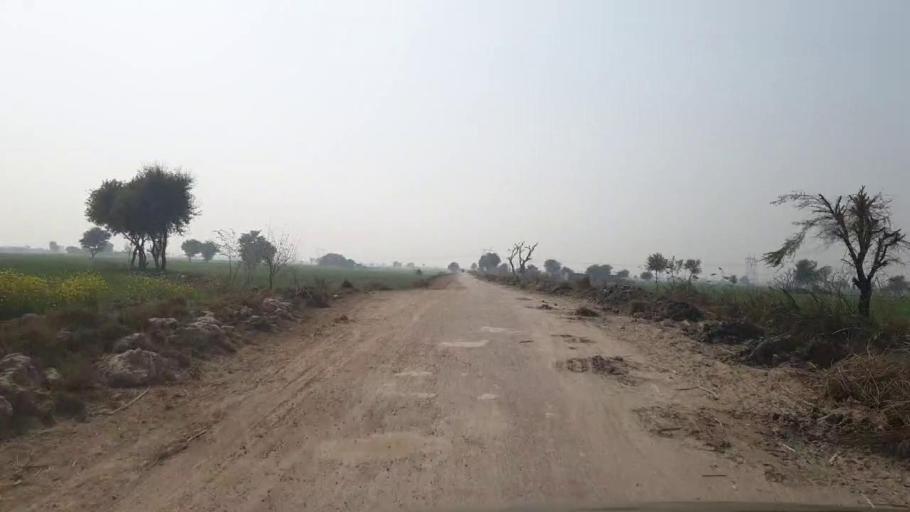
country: PK
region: Sindh
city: Hala
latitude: 25.9471
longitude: 68.4520
